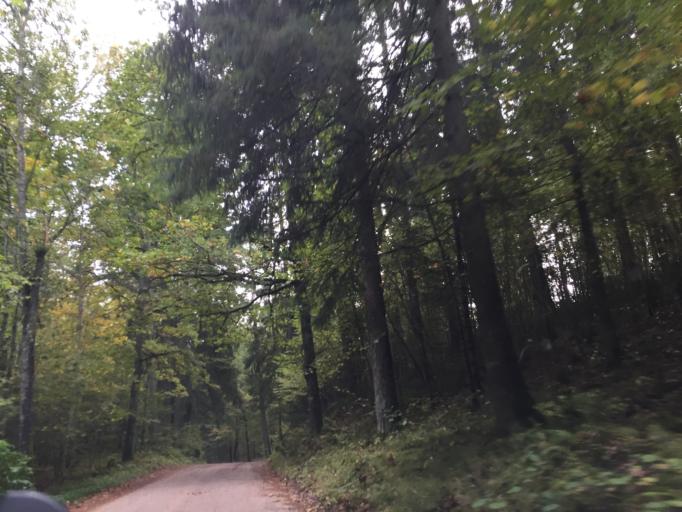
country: LV
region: Auces Novads
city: Auce
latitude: 56.5480
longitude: 23.0183
